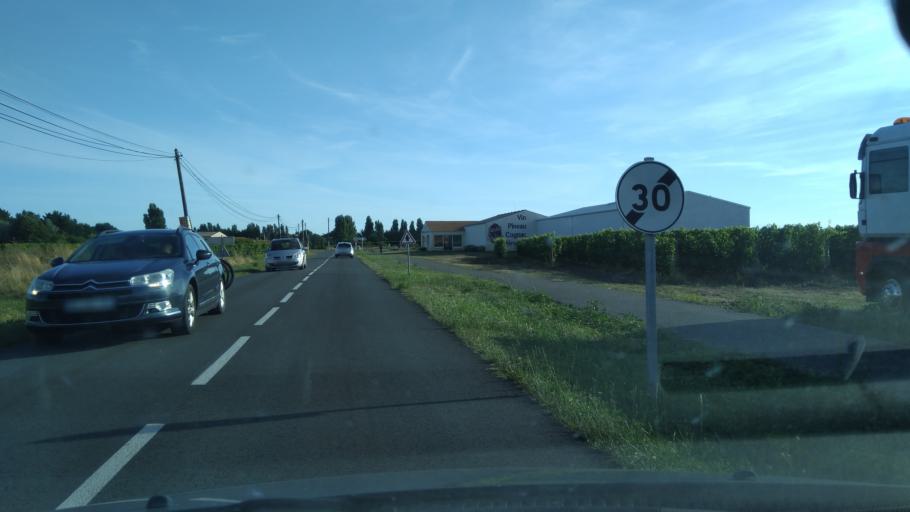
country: FR
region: Poitou-Charentes
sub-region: Departement de la Charente-Maritime
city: Dolus-d'Oleron
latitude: 45.9298
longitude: -1.3297
